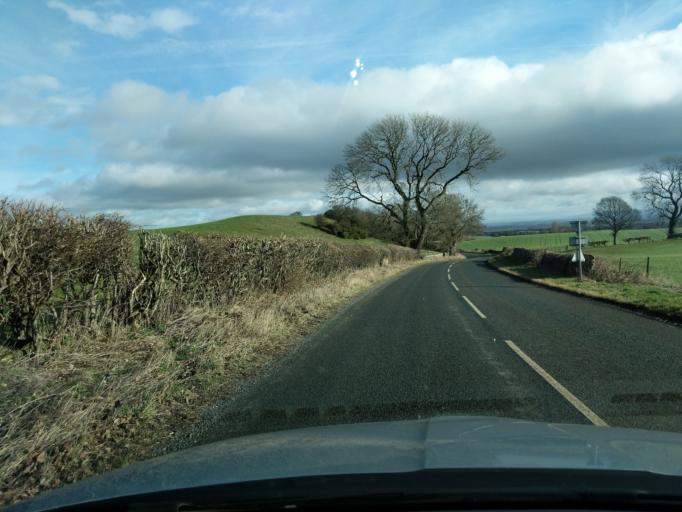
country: GB
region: England
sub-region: North Yorkshire
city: Catterick Garrison
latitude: 54.3485
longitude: -1.6927
